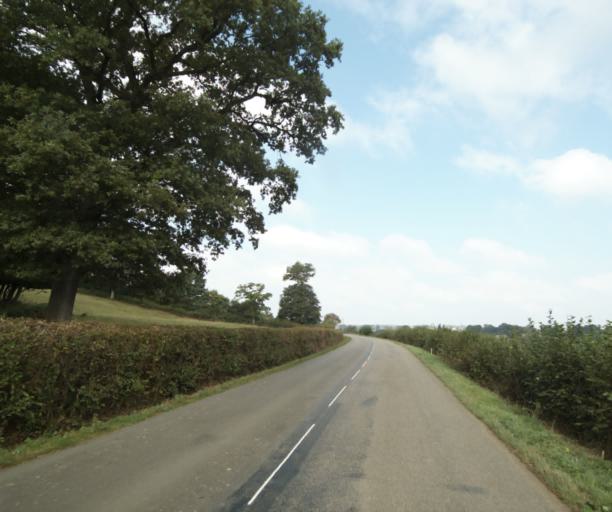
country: FR
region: Bourgogne
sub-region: Departement de Saone-et-Loire
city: Charolles
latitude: 46.4274
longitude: 4.3052
